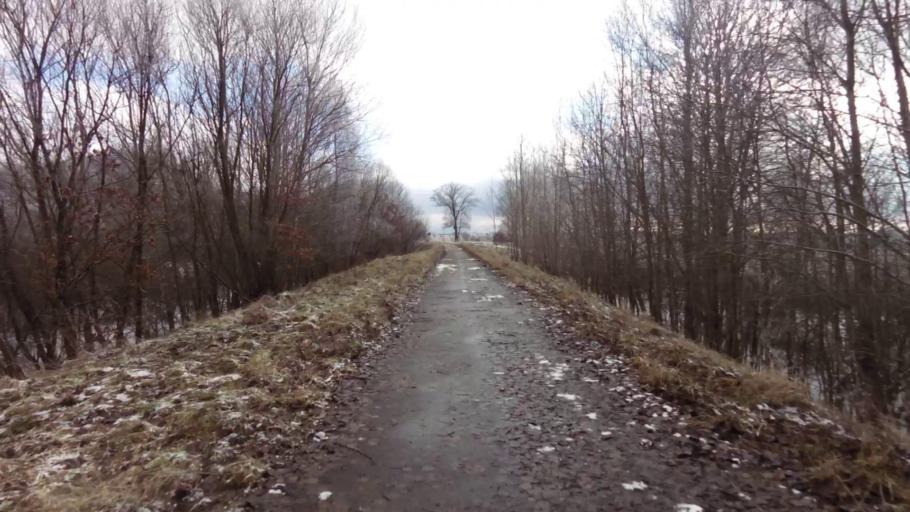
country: PL
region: West Pomeranian Voivodeship
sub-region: Powiat drawski
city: Zlocieniec
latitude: 53.6385
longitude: 16.0464
